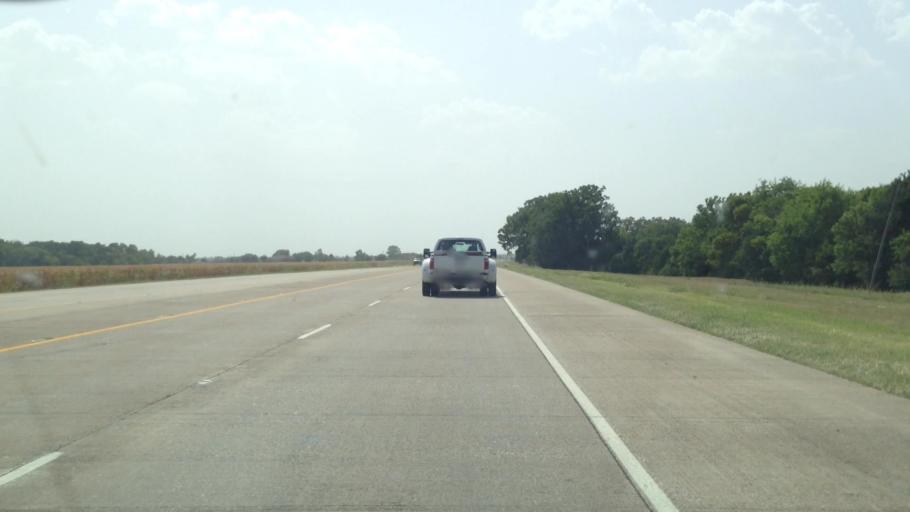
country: US
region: Texas
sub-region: Collin County
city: Princeton
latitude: 33.1645
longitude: -96.4443
